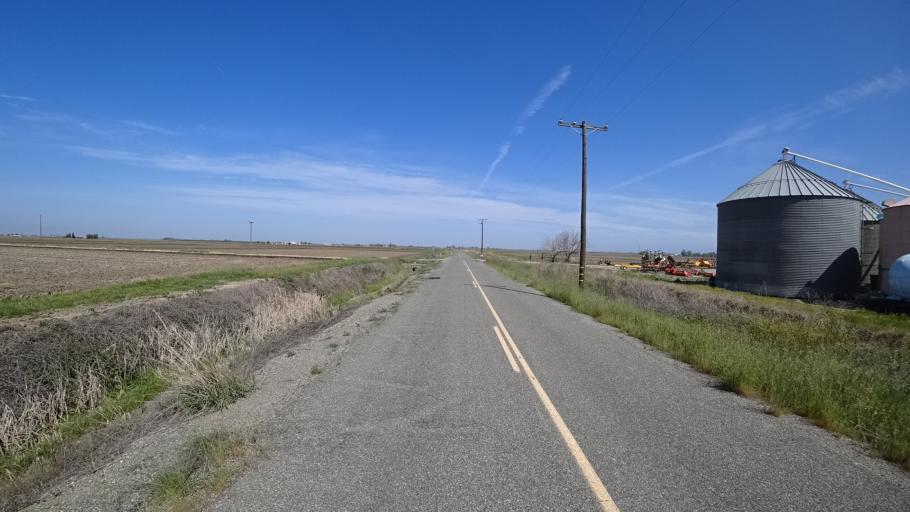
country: US
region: California
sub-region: Glenn County
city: Hamilton City
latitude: 39.5937
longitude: -122.0276
